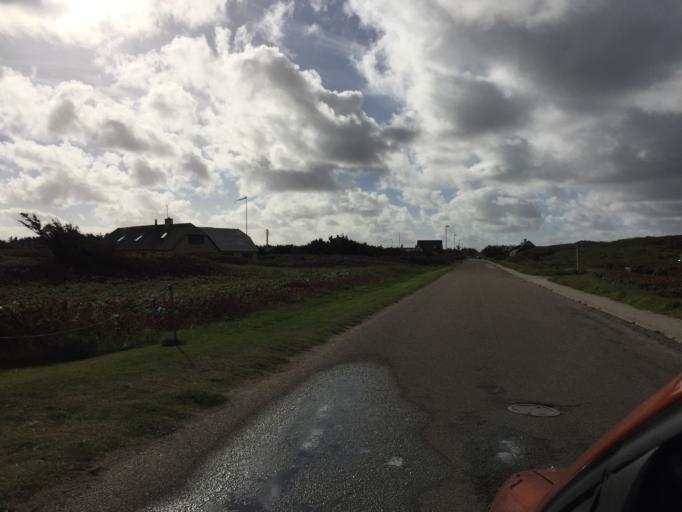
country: DK
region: North Denmark
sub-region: Thisted Kommune
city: Hanstholm
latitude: 57.0457
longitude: 8.5052
